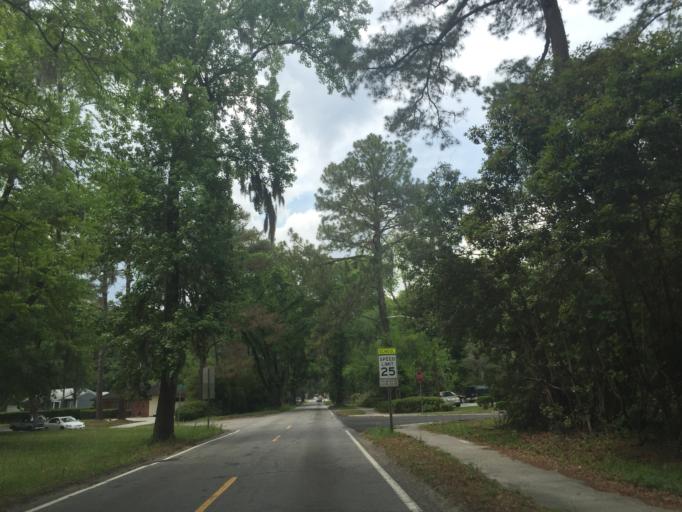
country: US
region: Georgia
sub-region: Chatham County
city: Thunderbolt
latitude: 32.0211
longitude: -81.0682
